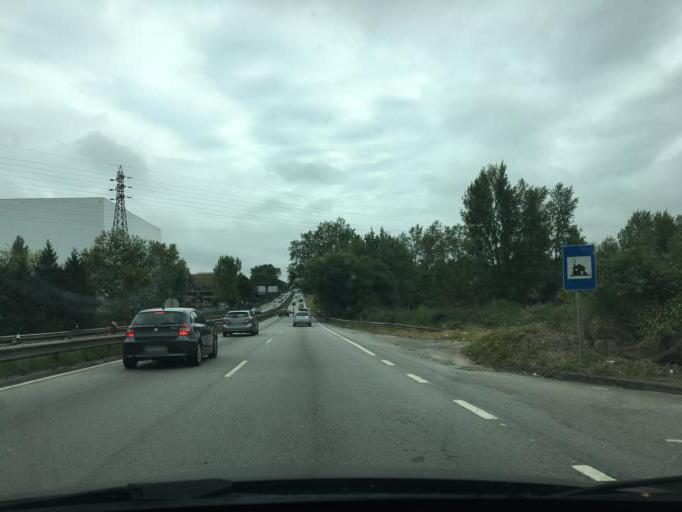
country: PT
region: Porto
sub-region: Maia
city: Leca do Bailio
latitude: 41.2181
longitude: -8.6271
